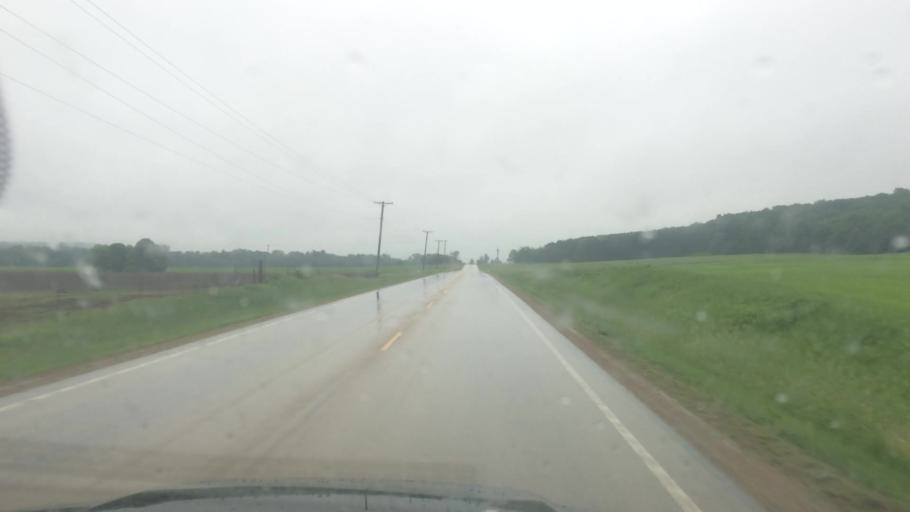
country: US
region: Wisconsin
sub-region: Waupaca County
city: Marion
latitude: 44.6103
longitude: -88.8936
